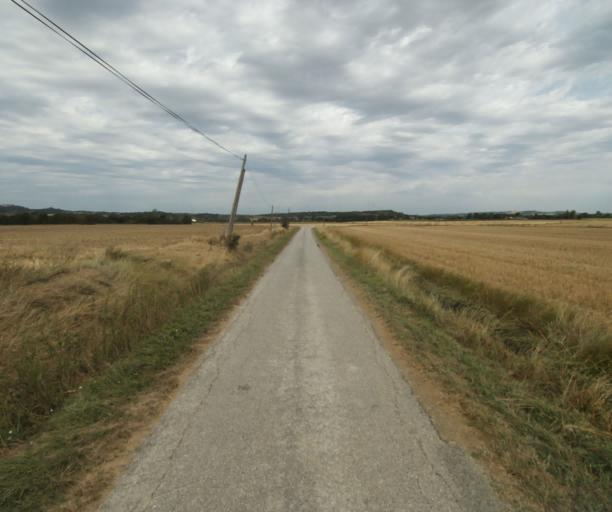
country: FR
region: Midi-Pyrenees
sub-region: Departement de la Haute-Garonne
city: Saint-Felix-Lauragais
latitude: 43.4376
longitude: 1.9344
